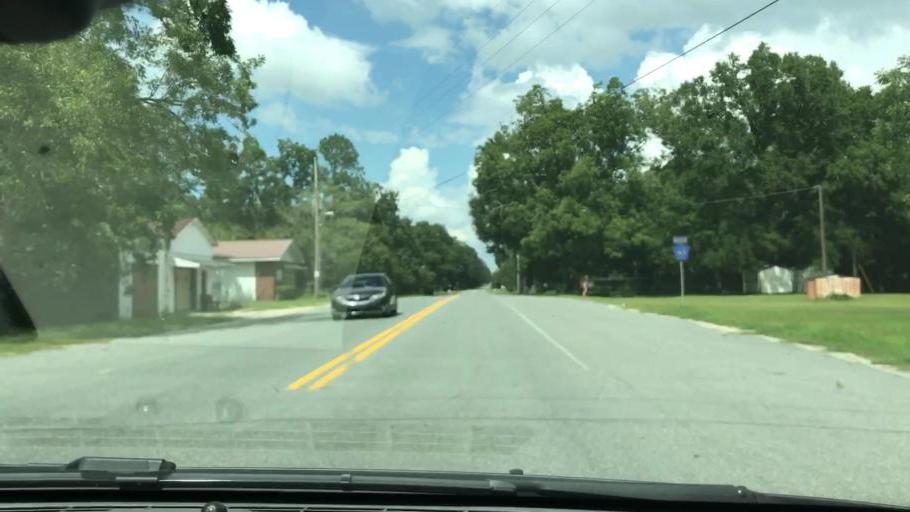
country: US
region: Florida
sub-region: Jackson County
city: Malone
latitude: 30.9268
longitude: -85.1186
